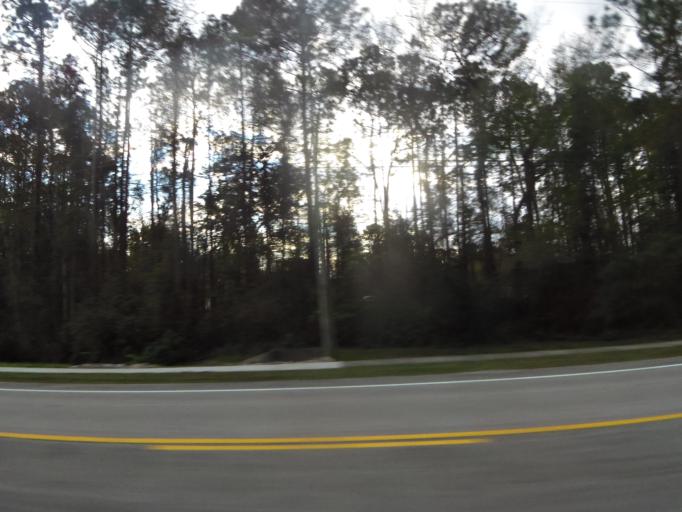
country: US
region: Florida
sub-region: Saint Johns County
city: Fruit Cove
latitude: 30.1817
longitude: -81.5696
